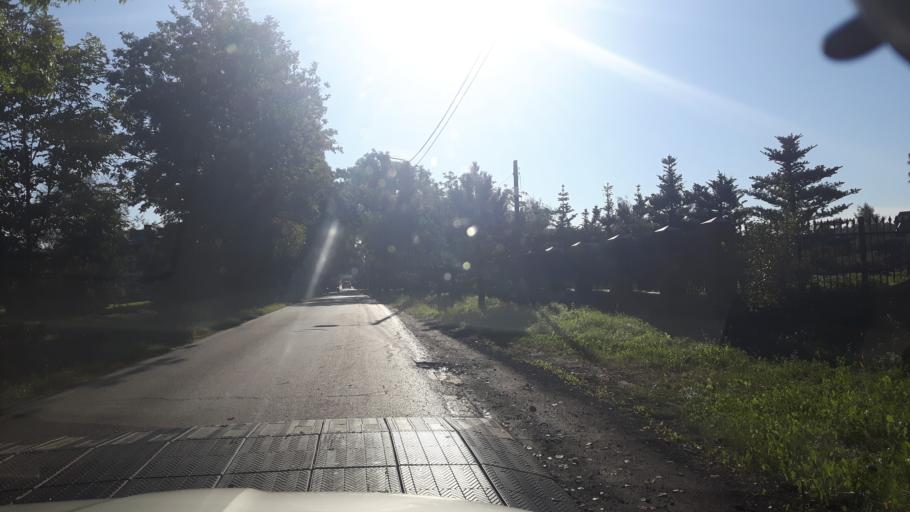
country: PL
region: Masovian Voivodeship
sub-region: Powiat legionowski
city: Stanislawow Pierwszy
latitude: 52.3514
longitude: 21.0225
